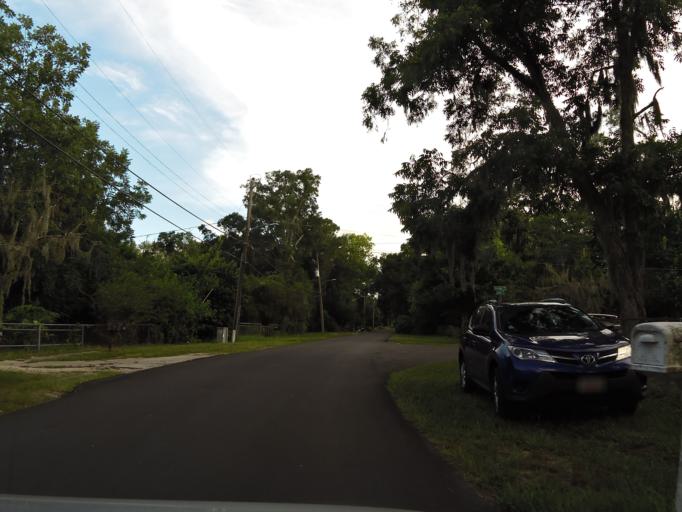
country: US
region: Florida
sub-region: Duval County
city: Jacksonville
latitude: 30.4316
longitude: -81.6896
